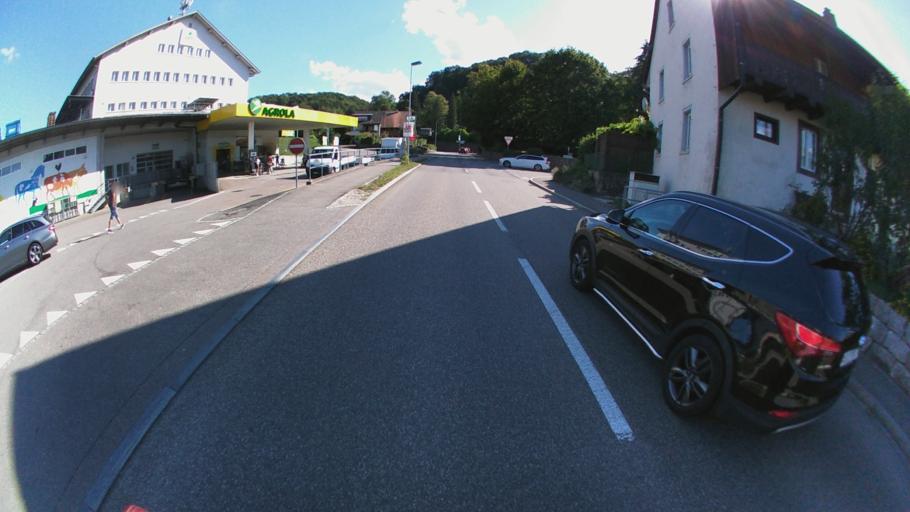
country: CH
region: Aargau
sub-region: Bezirk Laufenburg
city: Eiken
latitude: 47.5337
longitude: 7.9876
